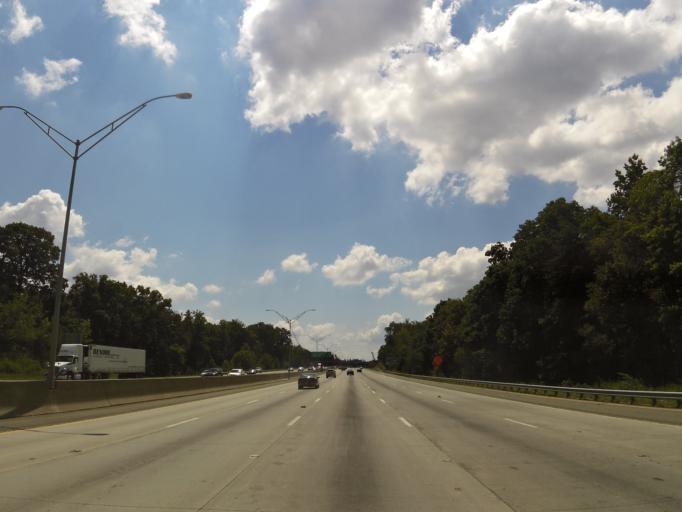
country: US
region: North Carolina
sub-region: Cabarrus County
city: Harrisburg
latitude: 35.3043
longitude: -80.7620
